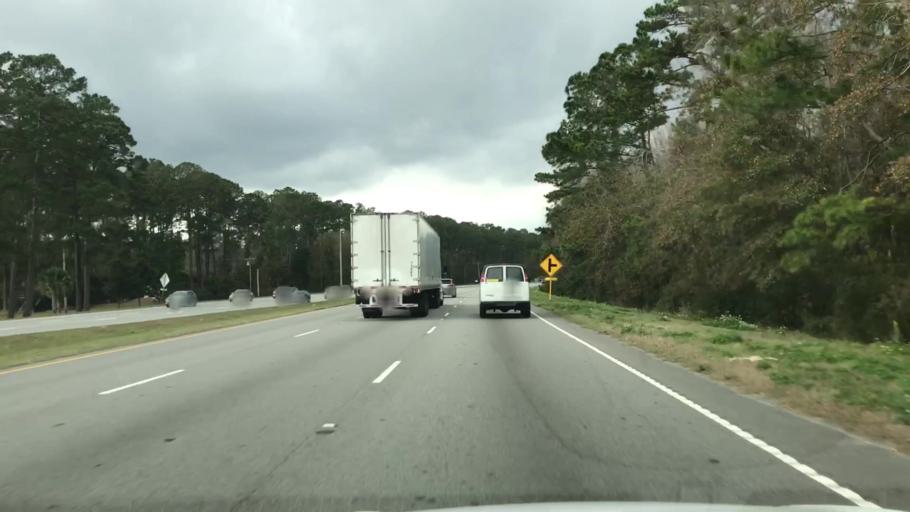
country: US
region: South Carolina
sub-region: Beaufort County
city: Bluffton
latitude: 32.2866
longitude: -80.8898
